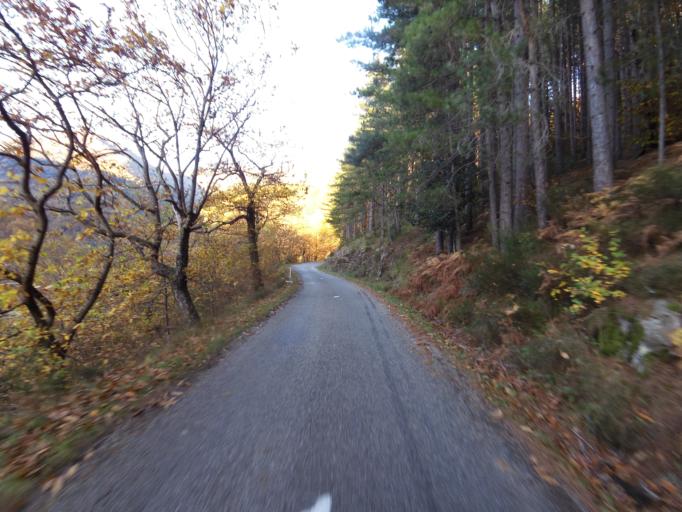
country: FR
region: Rhone-Alpes
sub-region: Departement de l'Ardeche
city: Les Vans
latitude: 44.5334
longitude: 4.0801
